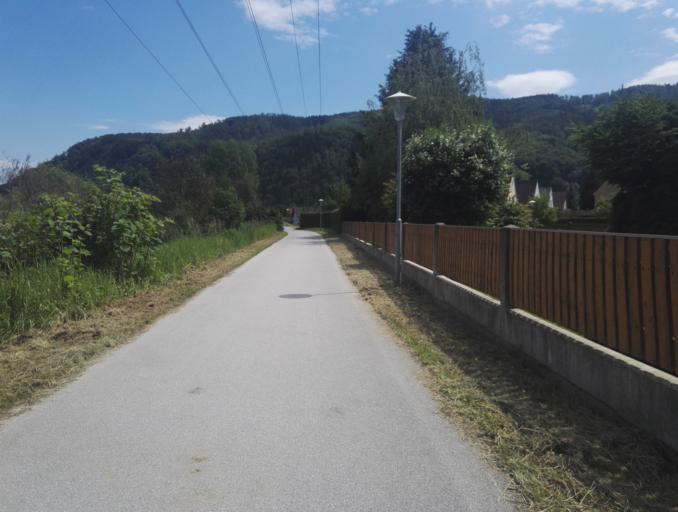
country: AT
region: Styria
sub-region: Politischer Bezirk Graz-Umgebung
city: Gratkorn
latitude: 47.1216
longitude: 15.3483
